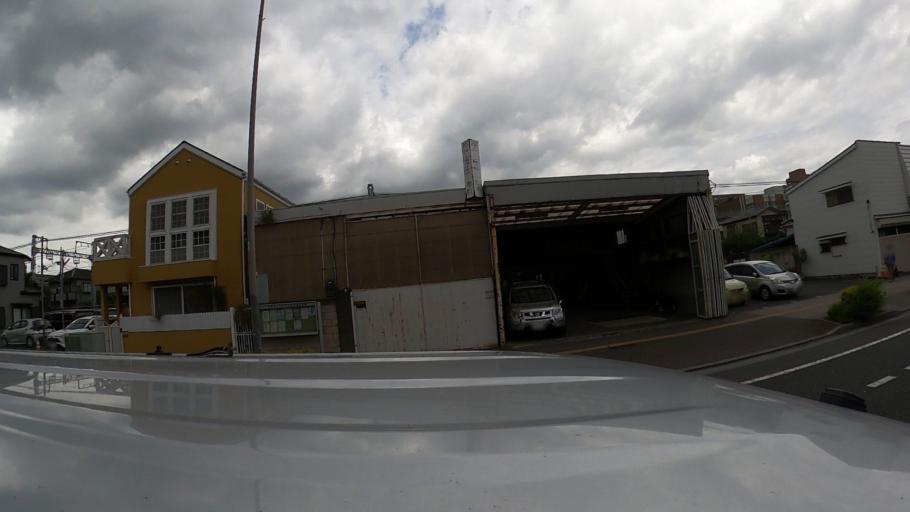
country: JP
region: Kanagawa
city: Yokohama
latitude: 35.4881
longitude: 139.6584
